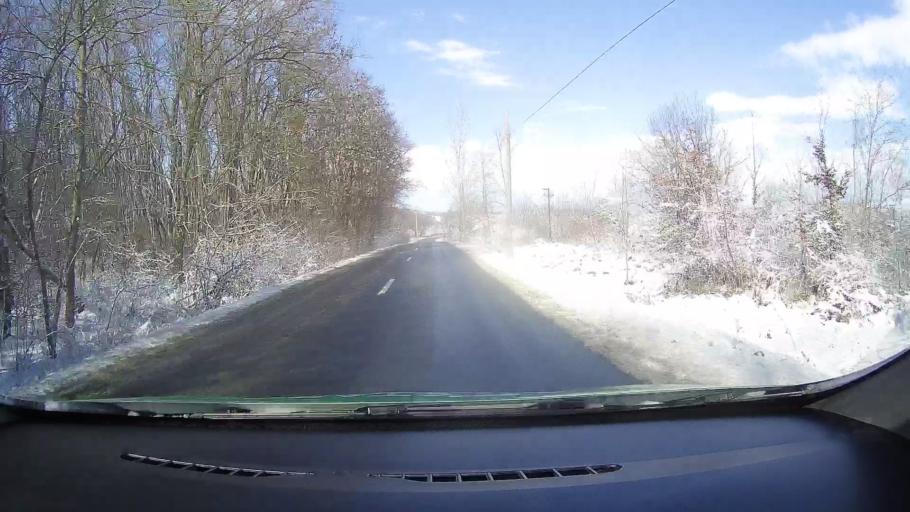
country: RO
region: Sibiu
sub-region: Comuna Nocrich
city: Nocrich
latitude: 45.8692
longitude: 24.4522
